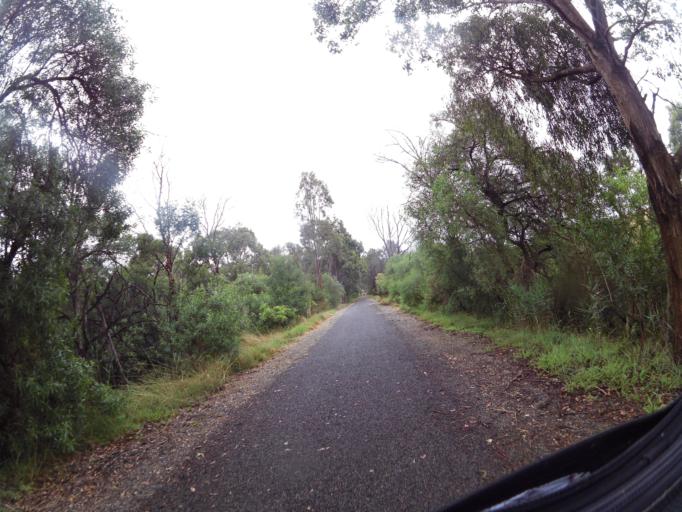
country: AU
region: Victoria
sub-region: East Gippsland
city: Bairnsdale
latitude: -37.8168
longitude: 147.7296
